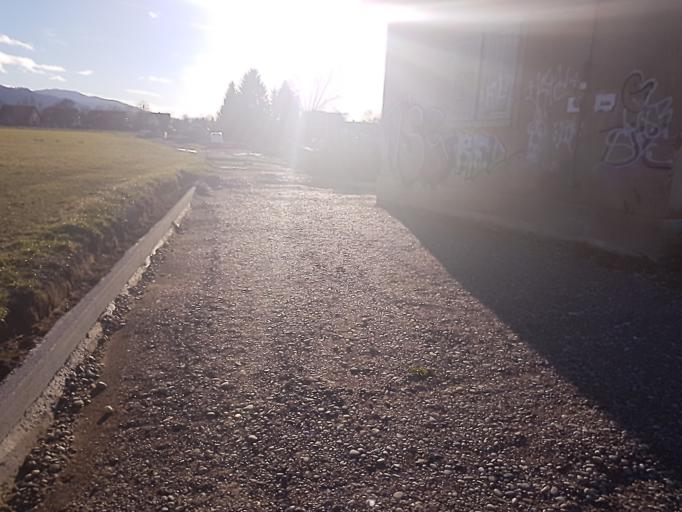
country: DE
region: Baden-Wuerttemberg
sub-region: Freiburg Region
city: Pfaffenweiler
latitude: 47.9203
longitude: 7.7359
